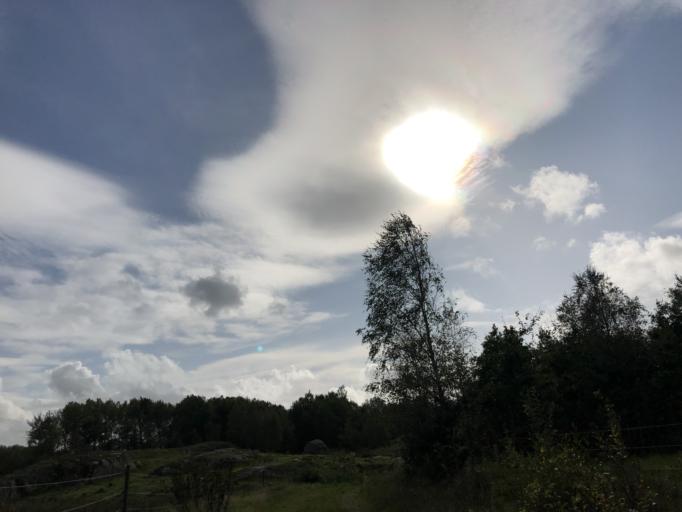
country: SE
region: Vaestra Goetaland
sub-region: Goteborg
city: Majorna
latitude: 57.7599
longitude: 11.8702
